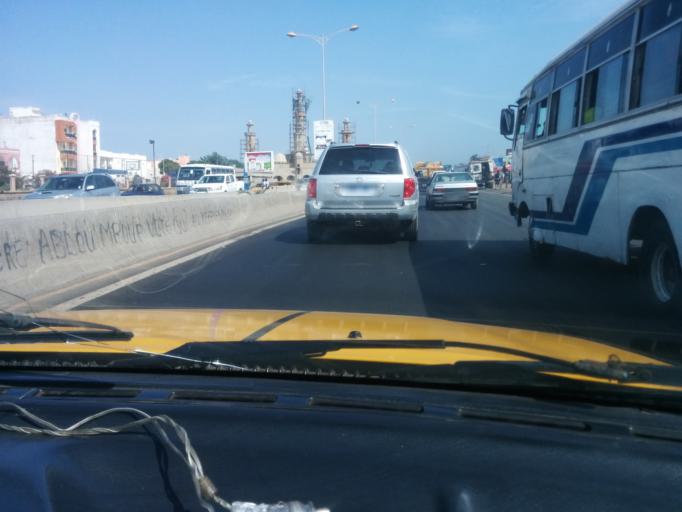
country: SN
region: Dakar
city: Grand Dakar
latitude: 14.7431
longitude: -17.4436
